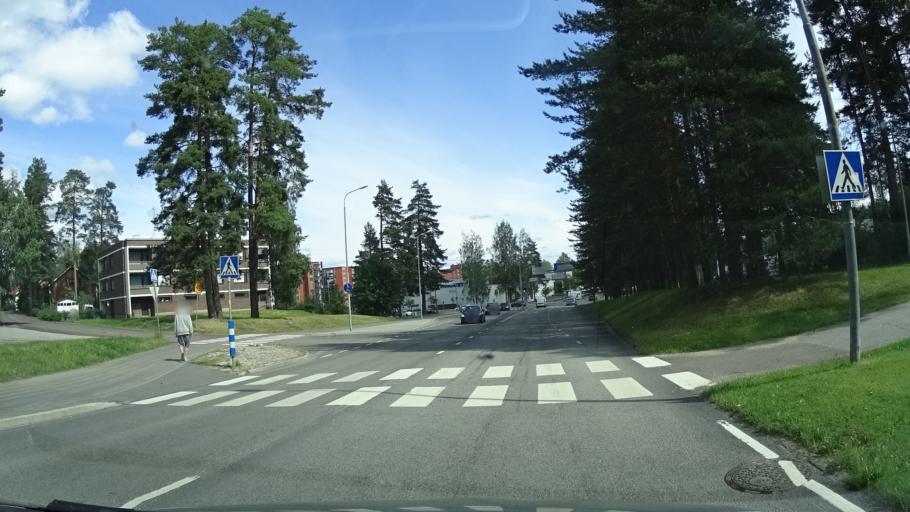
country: FI
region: Central Finland
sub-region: Jyvaeskylae
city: Jyvaeskylae
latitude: 62.2421
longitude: 25.7027
